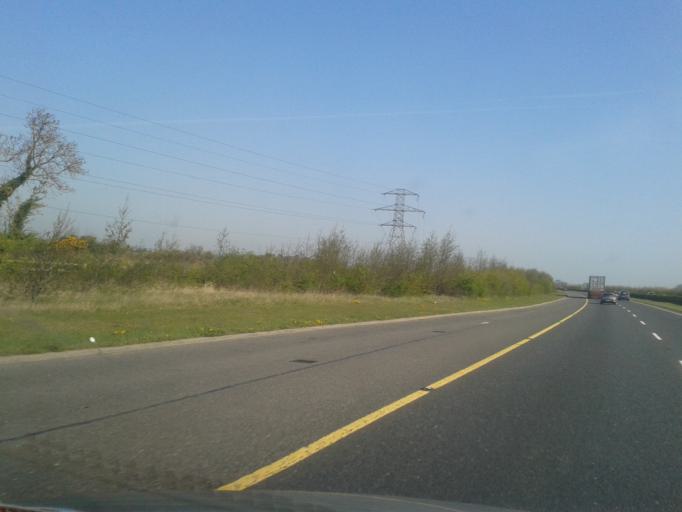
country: IE
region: Leinster
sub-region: Fingal County
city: Swords
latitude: 53.4961
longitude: -6.2010
